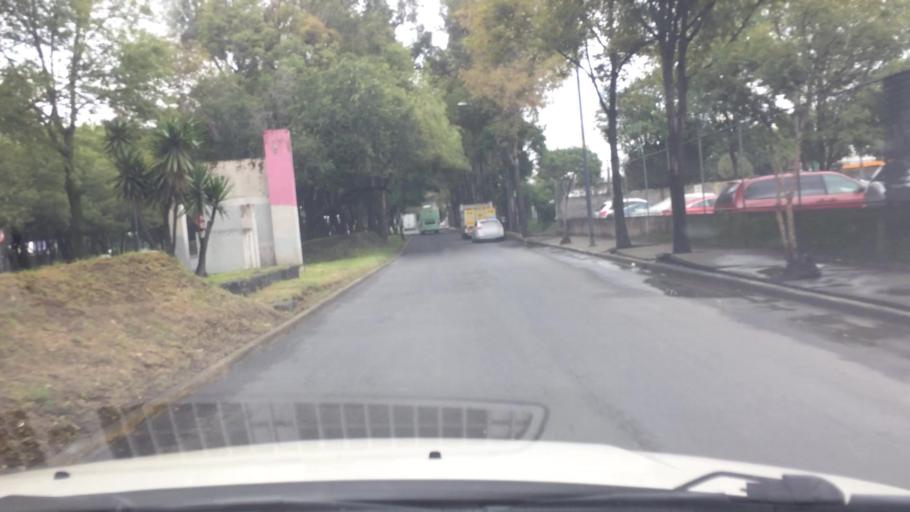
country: MX
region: Mexico City
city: Xochimilco
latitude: 19.2853
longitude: -99.1257
